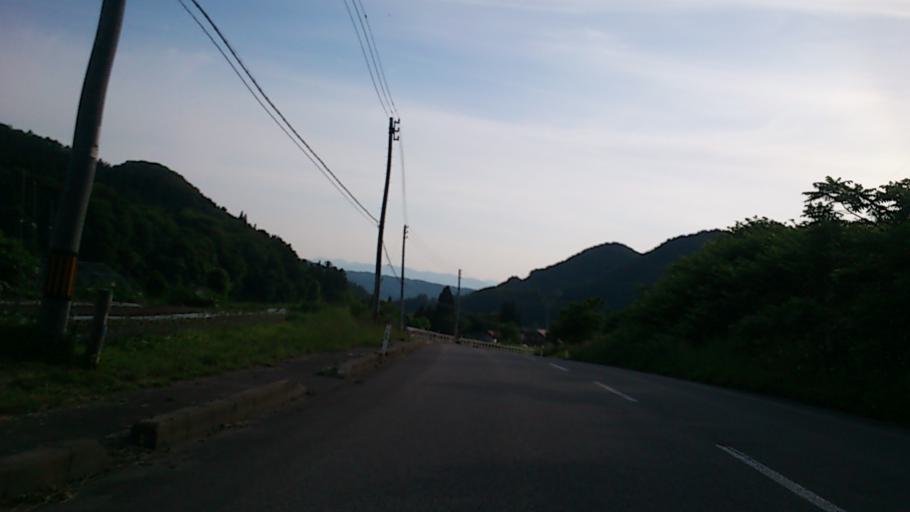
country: JP
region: Aomori
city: Kuroishi
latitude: 40.6361
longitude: 140.7208
